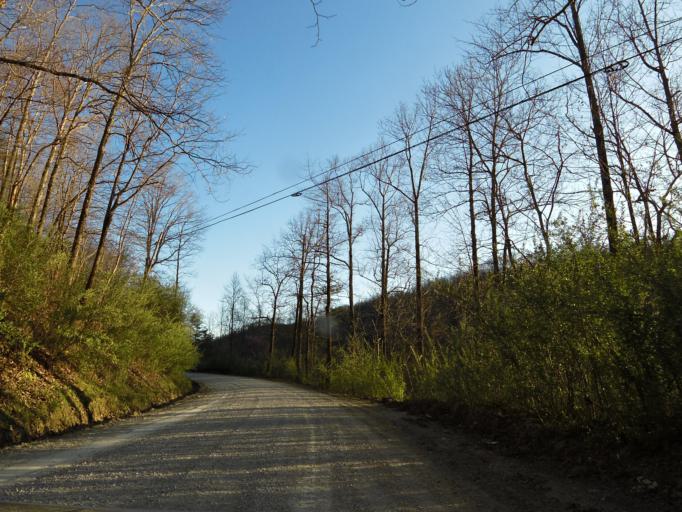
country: US
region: Tennessee
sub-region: Campbell County
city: Caryville
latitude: 36.2233
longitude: -84.3259
